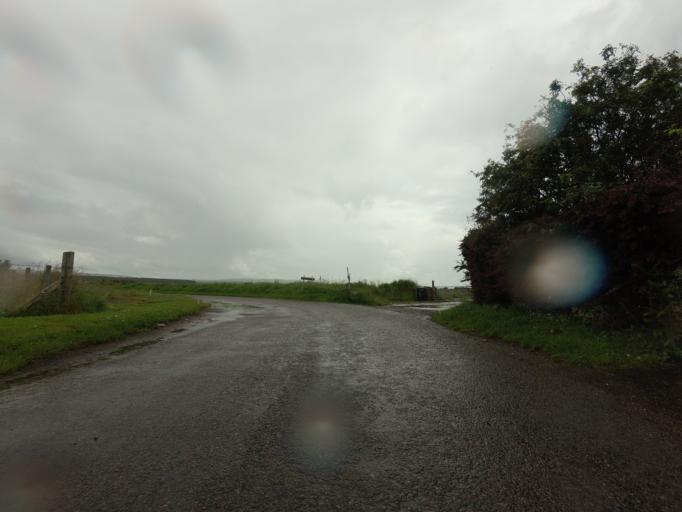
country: GB
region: Scotland
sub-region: Moray
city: Fochabers
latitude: 57.6593
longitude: -3.0733
